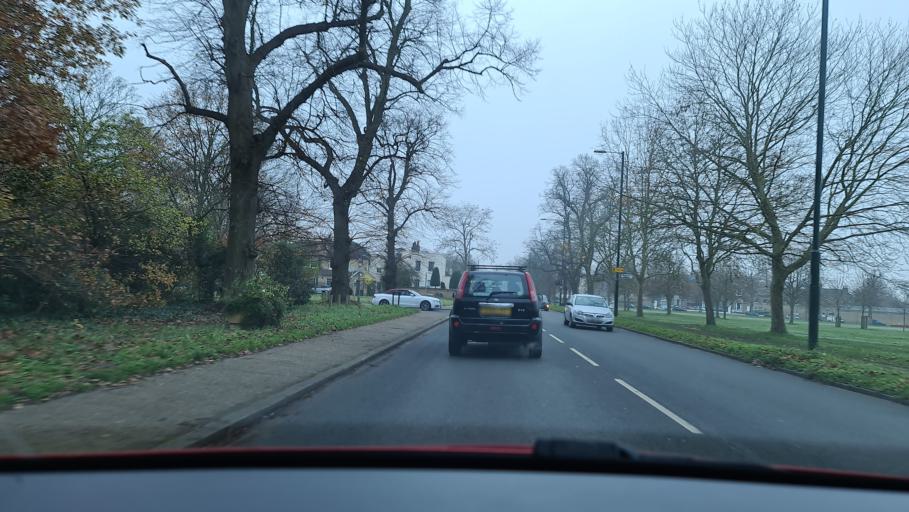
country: GB
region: England
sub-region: Greater London
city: Kingston upon Thames
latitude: 51.4348
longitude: -0.3057
